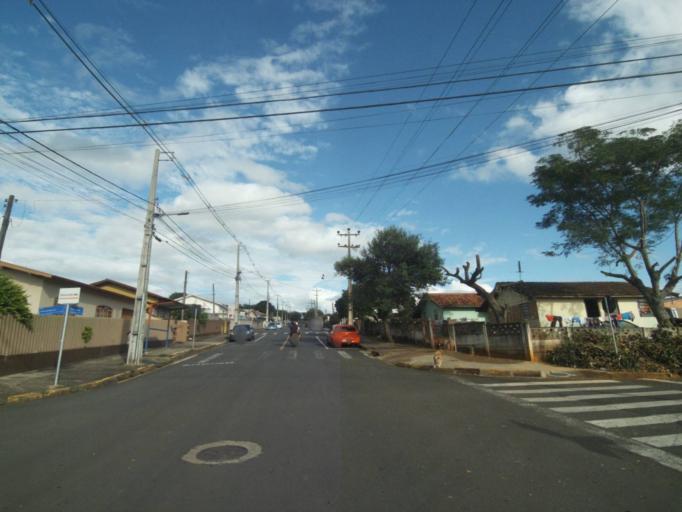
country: BR
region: Parana
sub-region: Telemaco Borba
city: Telemaco Borba
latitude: -24.3381
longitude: -50.6144
